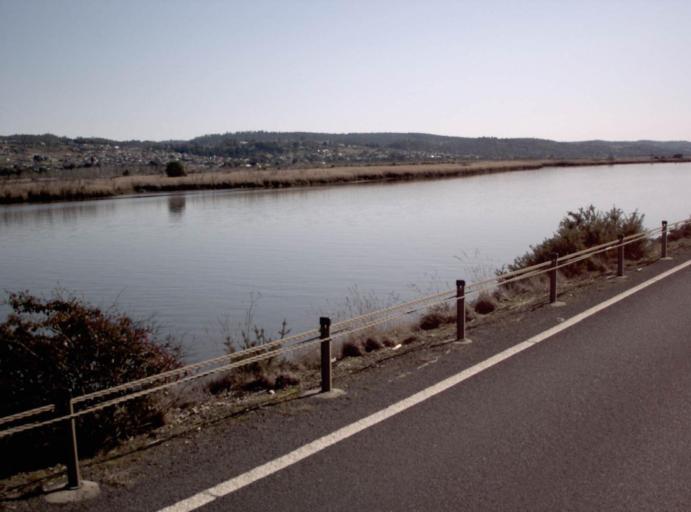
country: AU
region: Tasmania
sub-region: Launceston
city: Newnham
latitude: -41.4093
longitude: 147.1262
